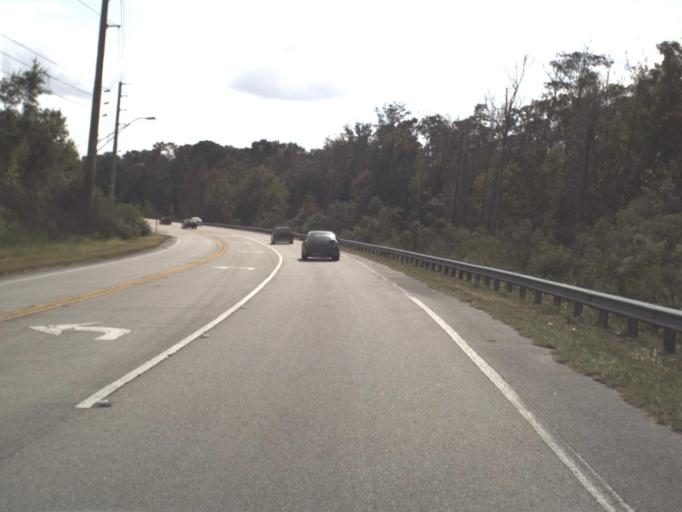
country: US
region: Florida
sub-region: Osceola County
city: Campbell
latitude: 28.2010
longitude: -81.4754
